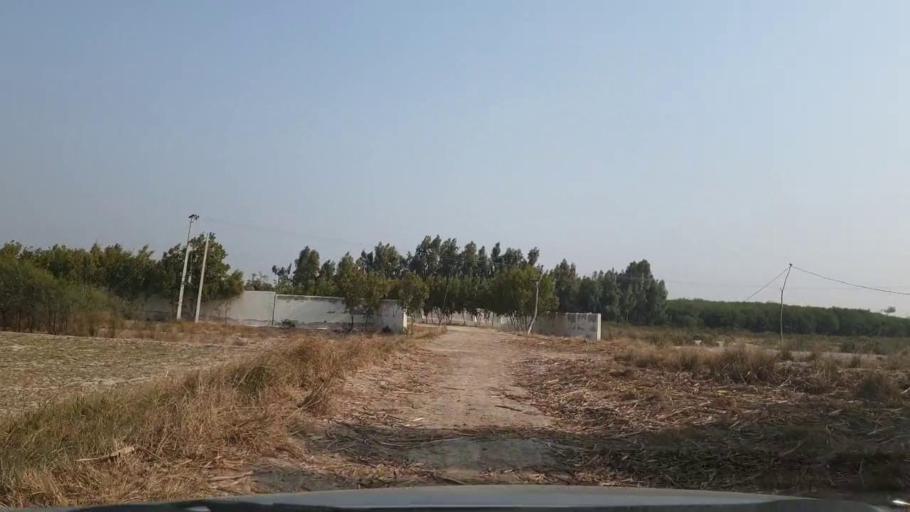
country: PK
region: Sindh
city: Matiari
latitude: 25.6439
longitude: 68.5757
